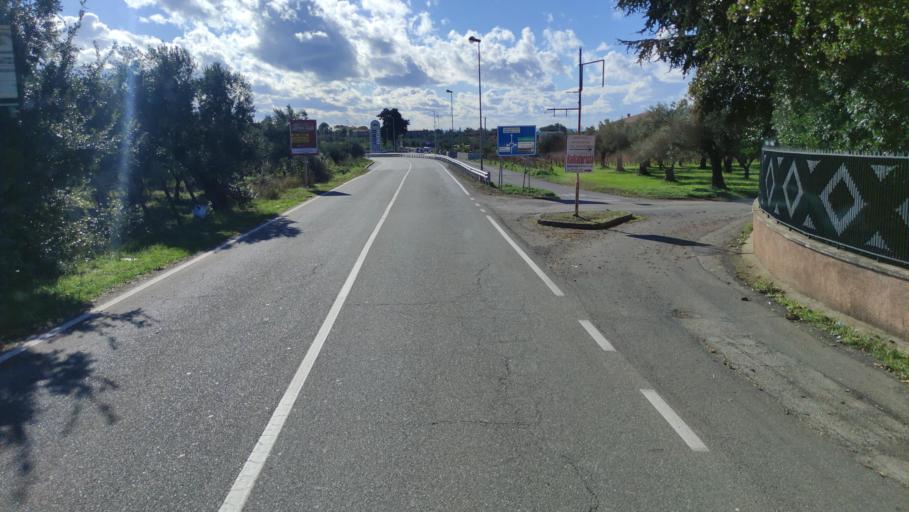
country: IT
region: Calabria
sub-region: Provincia di Catanzaro
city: Santa Eufemia Lamezia
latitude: 38.9259
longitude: 16.2837
